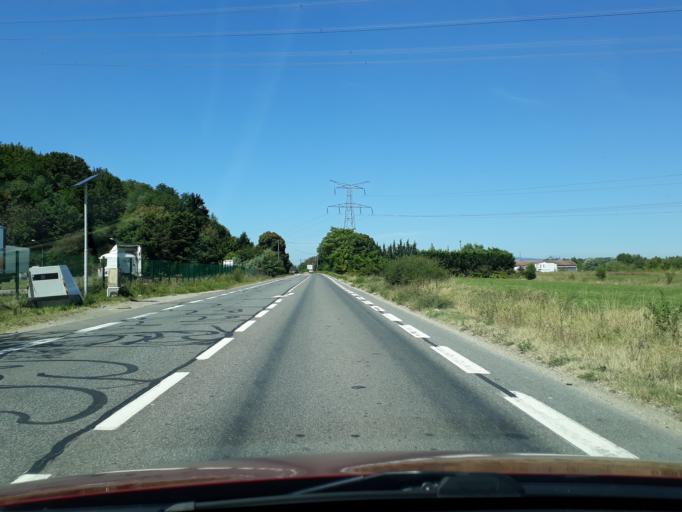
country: FR
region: Rhone-Alpes
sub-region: Departement du Rhone
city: Toussieu
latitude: 45.6653
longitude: 4.9916
